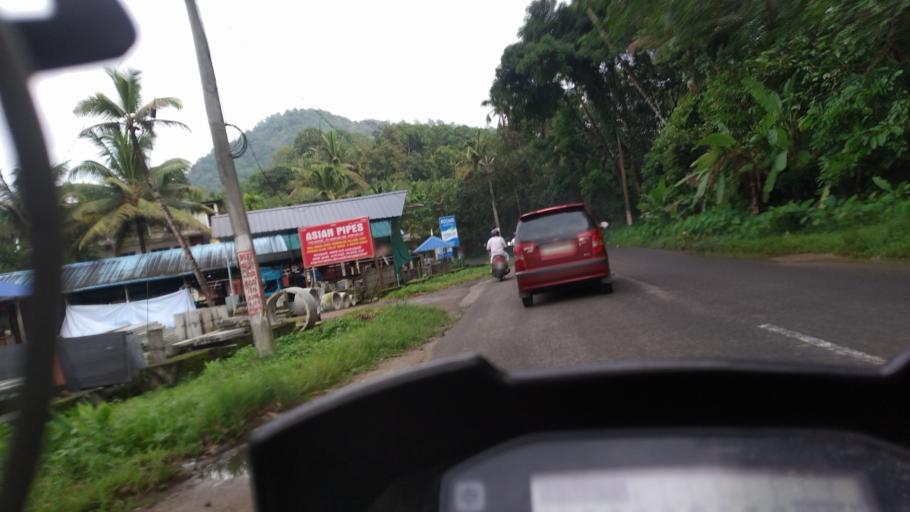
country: IN
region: Kerala
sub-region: Idukki
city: Kuttampuzha
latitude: 10.0507
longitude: 76.7458
